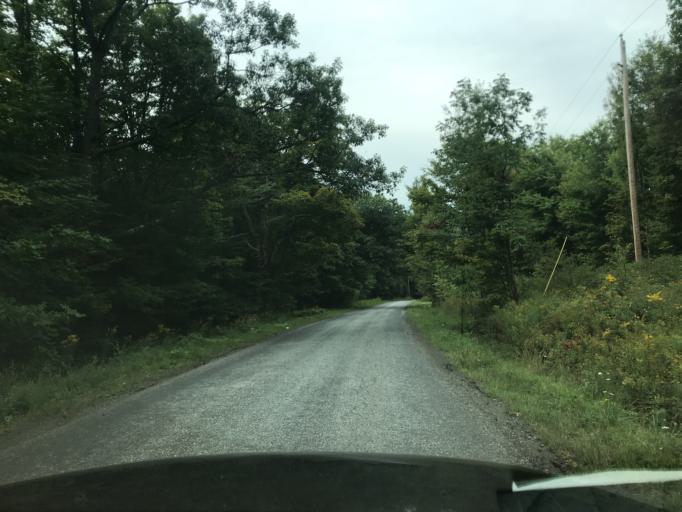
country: US
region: New York
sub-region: Otsego County
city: Worcester
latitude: 42.5908
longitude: -74.6964
